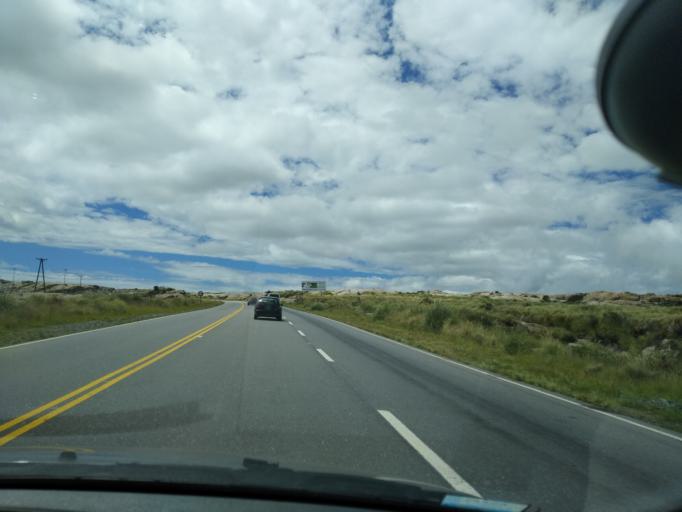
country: AR
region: Cordoba
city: Mina Clavero
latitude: -31.6152
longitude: -64.8808
